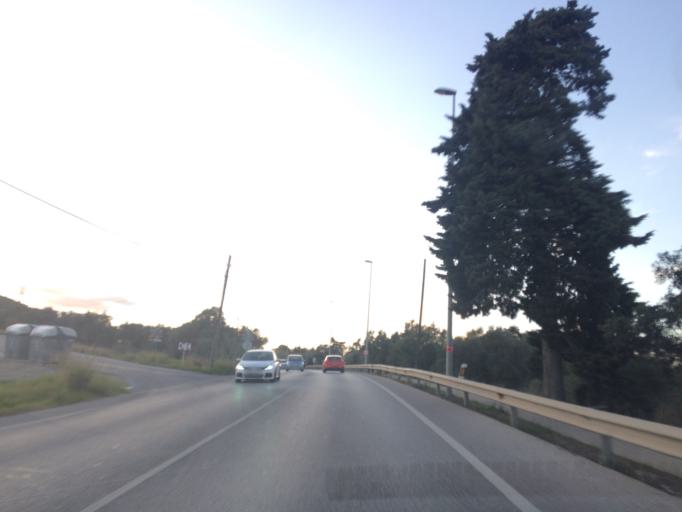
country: ES
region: Andalusia
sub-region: Provincia de Malaga
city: Torremolinos
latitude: 36.6620
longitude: -4.5076
